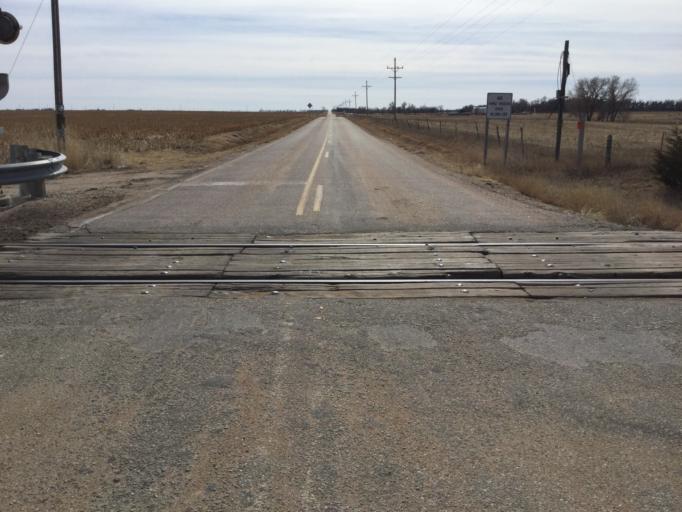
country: US
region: Kansas
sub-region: Rice County
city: Lyons
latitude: 38.5145
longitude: -98.3497
